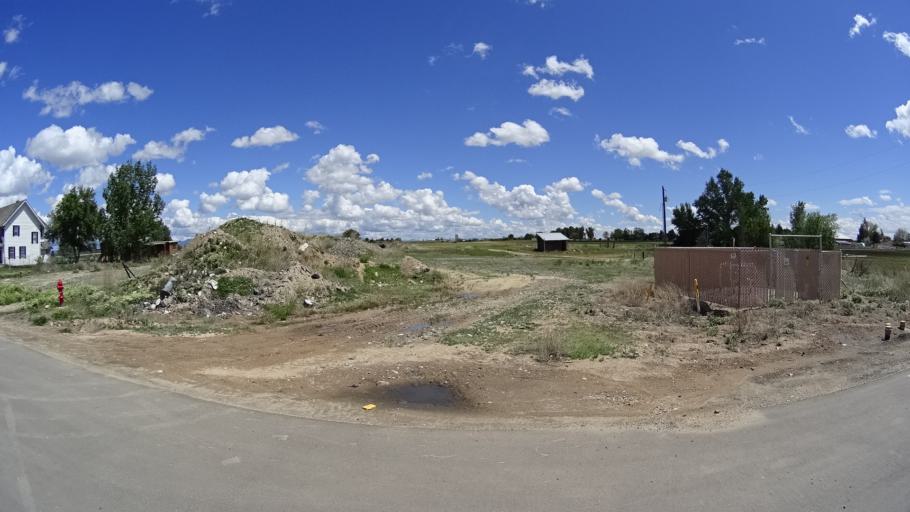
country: US
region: Idaho
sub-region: Ada County
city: Kuna
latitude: 43.5491
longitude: -116.4338
